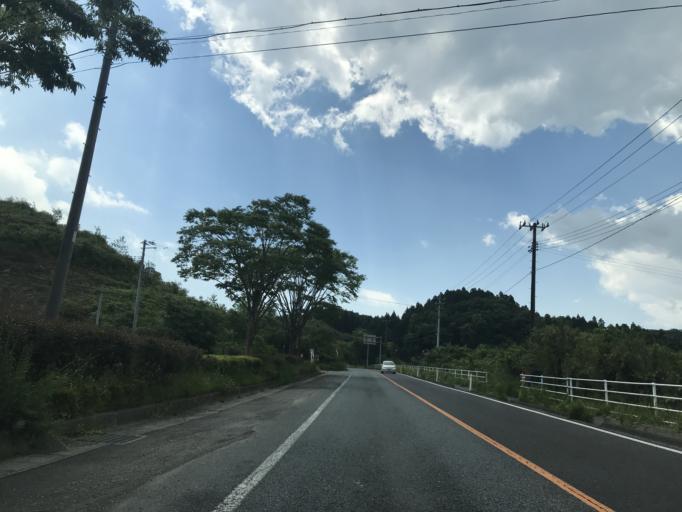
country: JP
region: Miyagi
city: Matsushima
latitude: 38.4200
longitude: 141.0591
